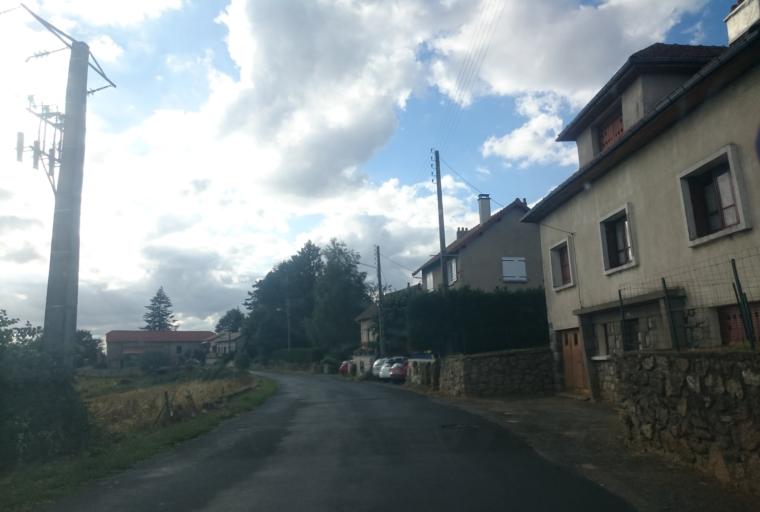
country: FR
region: Auvergne
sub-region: Departement du Cantal
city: Saint-Mamet-la-Salvetat
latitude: 44.8584
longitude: 2.3010
